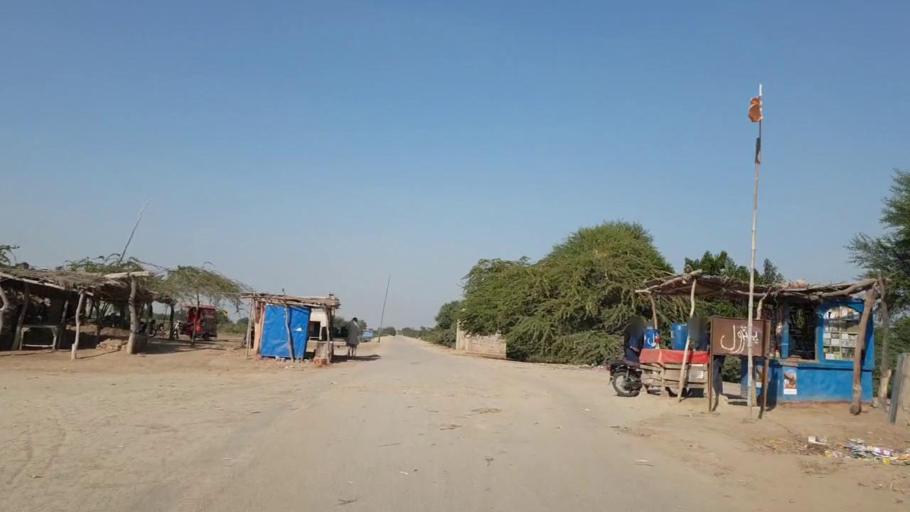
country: PK
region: Sindh
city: Digri
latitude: 25.0344
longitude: 69.1050
